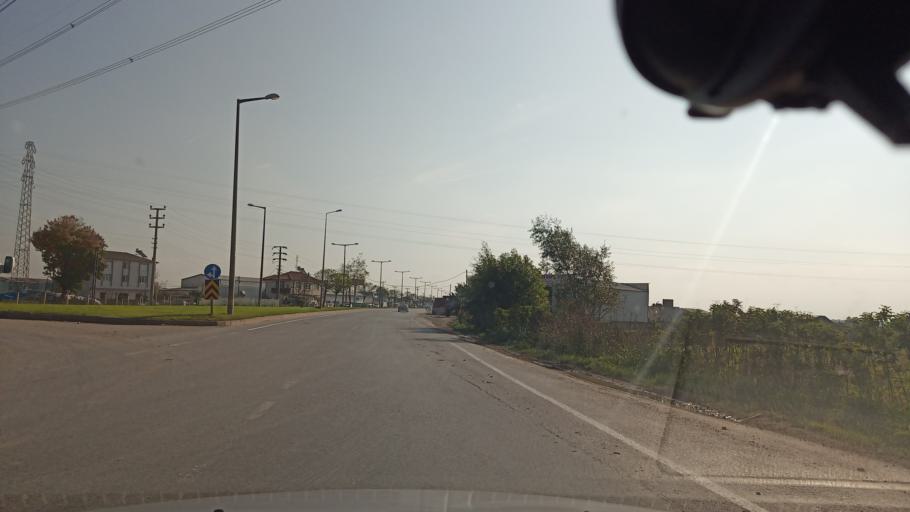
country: TR
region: Sakarya
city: Adapazari
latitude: 40.8216
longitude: 30.3969
